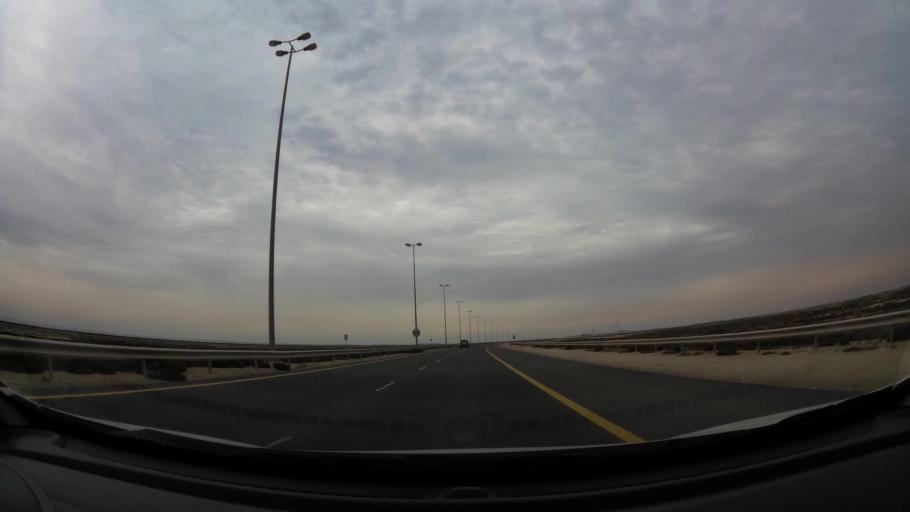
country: BH
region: Central Governorate
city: Dar Kulayb
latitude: 25.8657
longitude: 50.5839
